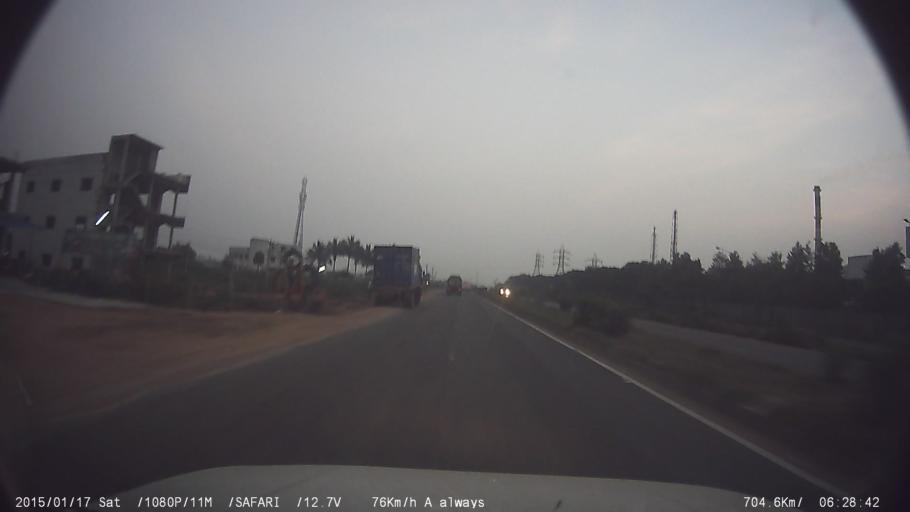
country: IN
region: Tamil Nadu
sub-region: Kancheepuram
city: Sriperumbudur
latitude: 12.9363
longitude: 79.9116
